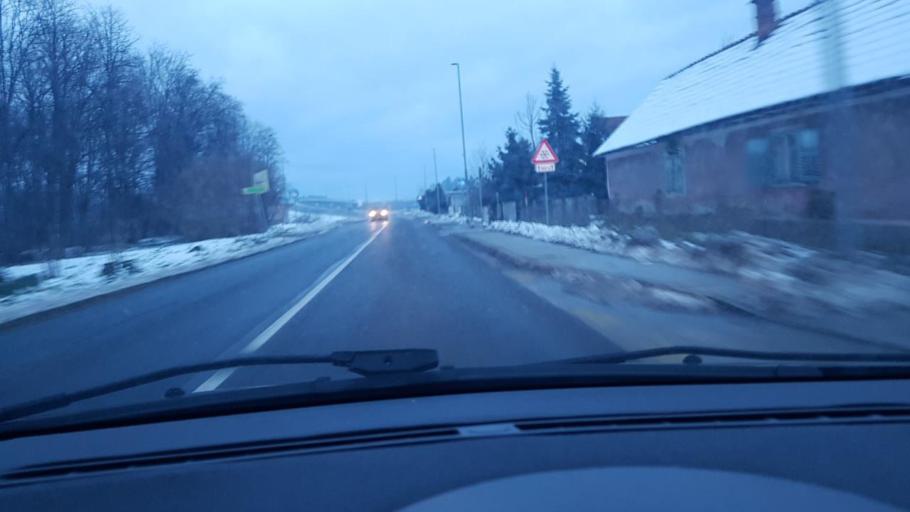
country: SI
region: Hajdina
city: Spodnja Hajdina
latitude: 46.3981
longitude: 15.8239
